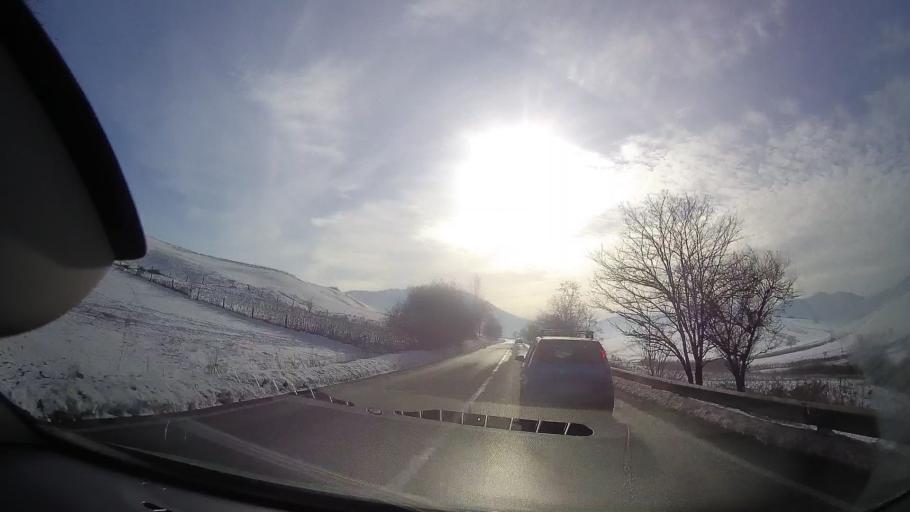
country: RO
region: Neamt
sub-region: Comuna Garcina
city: Garcina
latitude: 46.9857
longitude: 26.3596
